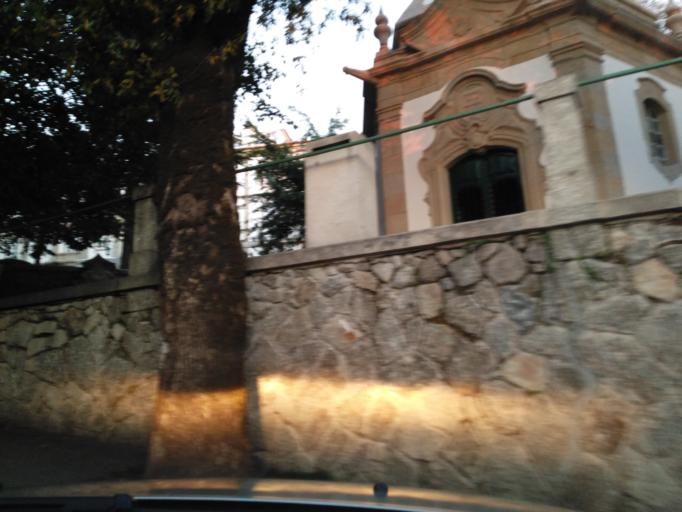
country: PT
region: Braga
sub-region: Braga
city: Adaufe
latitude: 41.5556
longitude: -8.3773
